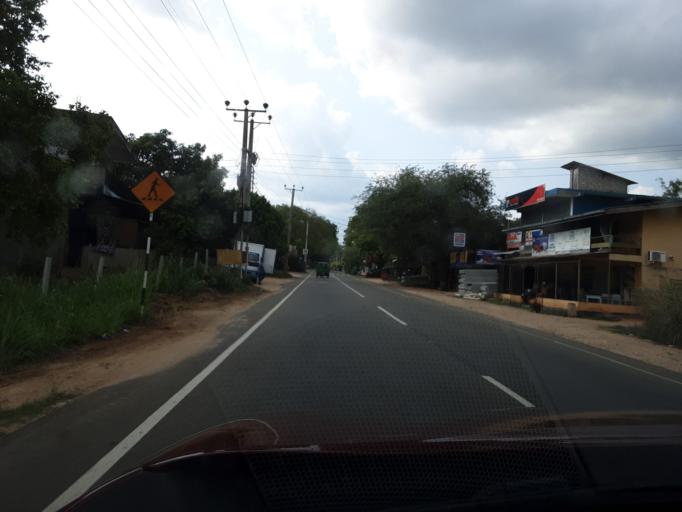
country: LK
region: Uva
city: Haputale
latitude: 6.5214
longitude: 81.1253
